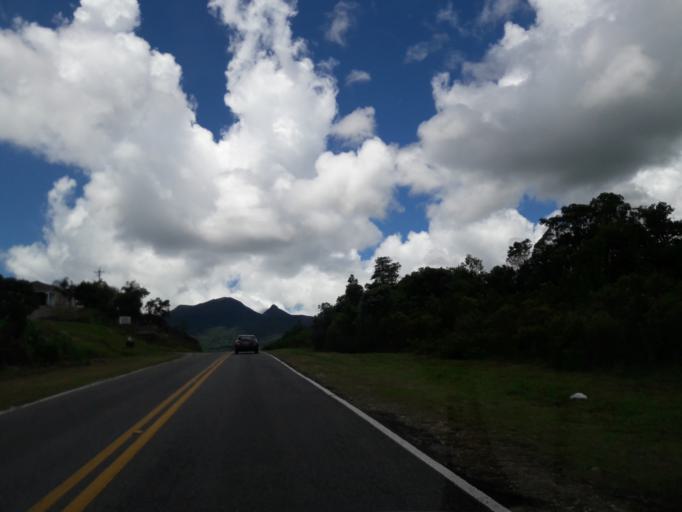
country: BR
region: Parana
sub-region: Campina Grande Do Sul
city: Campina Grande do Sul
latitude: -25.3133
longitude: -48.9314
